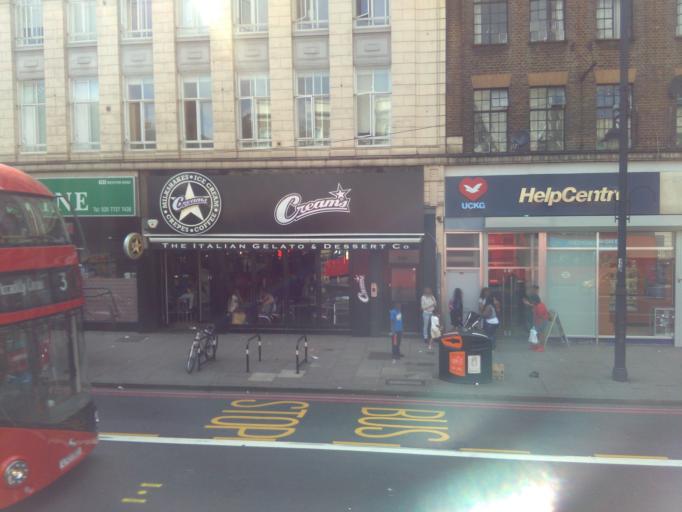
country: GB
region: England
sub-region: Greater London
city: Brixton
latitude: 51.4656
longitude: -0.1138
